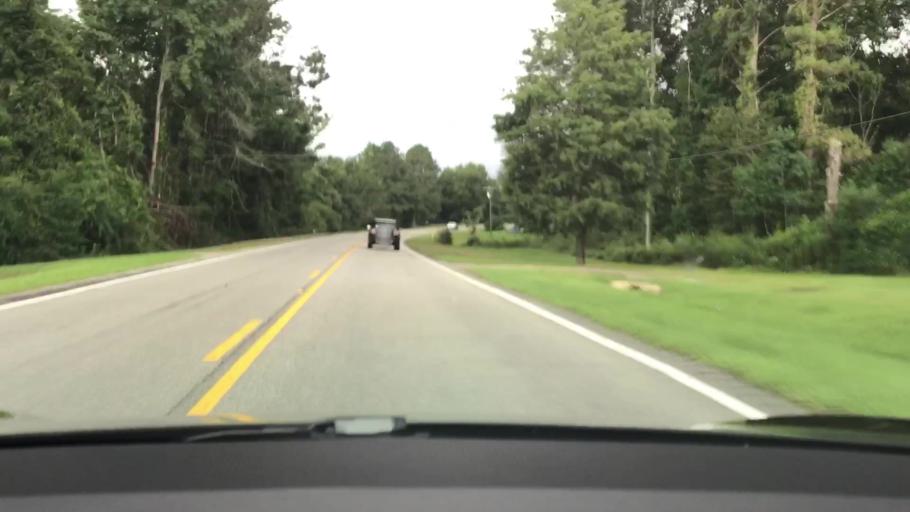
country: US
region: Alabama
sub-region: Coffee County
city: Elba
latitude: 31.4740
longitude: -86.0610
